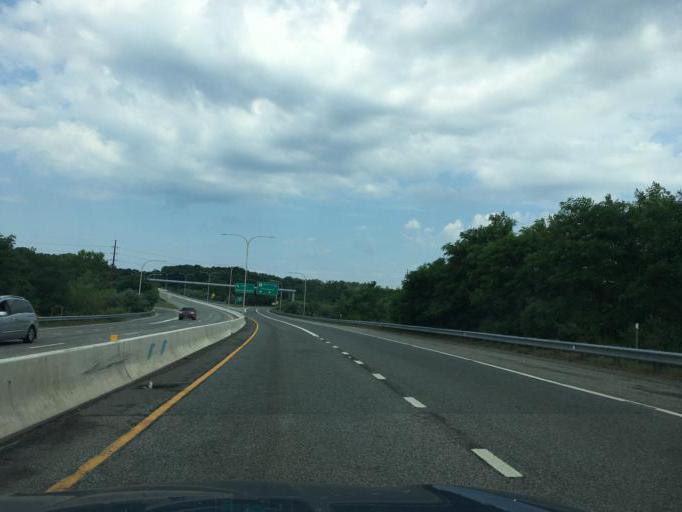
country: US
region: Rhode Island
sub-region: Kent County
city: East Greenwich
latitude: 41.6290
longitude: -71.4813
